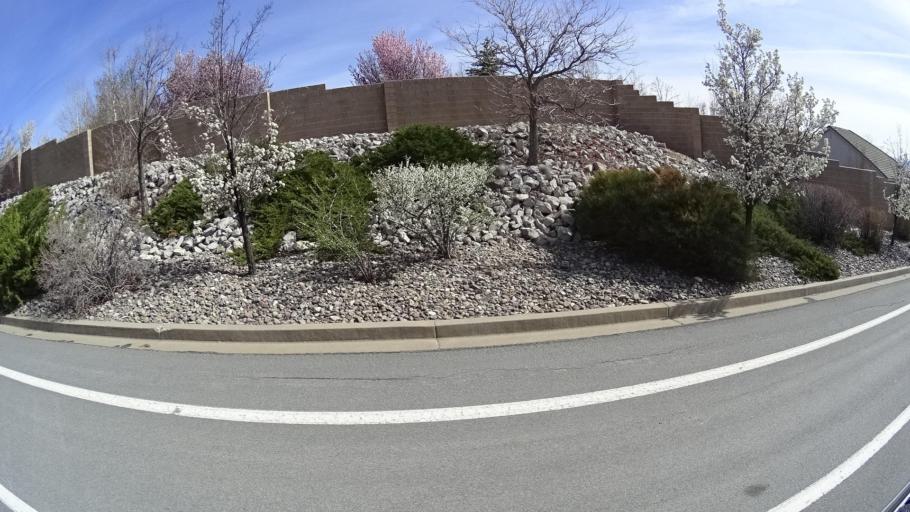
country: US
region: Nevada
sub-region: Washoe County
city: Mogul
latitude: 39.5416
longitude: -119.8896
